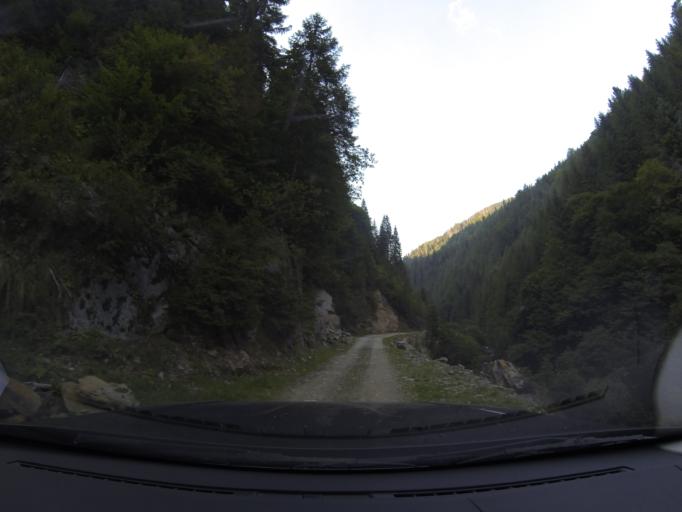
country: RO
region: Brasov
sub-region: Oras Victoria
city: Victoria
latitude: 45.5298
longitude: 24.6760
